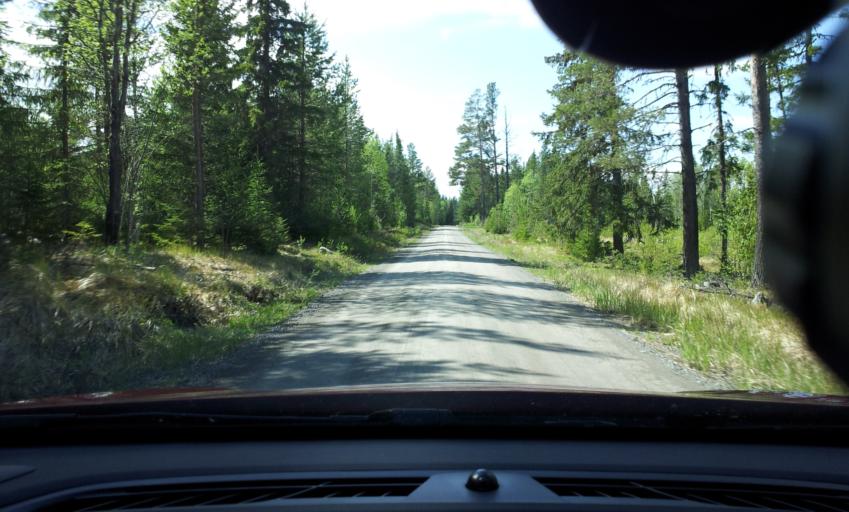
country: SE
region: Jaemtland
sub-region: Bergs Kommun
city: Hoverberg
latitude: 62.9548
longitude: 14.5389
